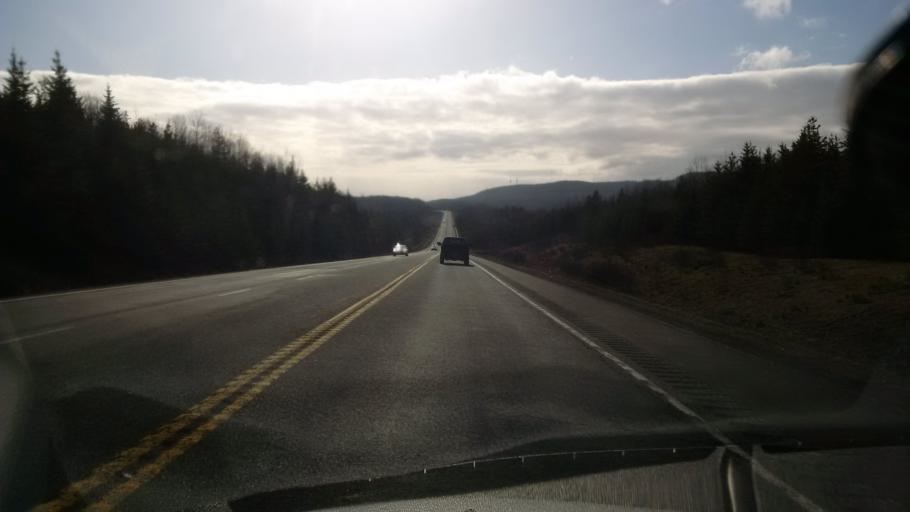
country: CA
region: Nova Scotia
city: Antigonish
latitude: 45.5874
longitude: -62.2972
